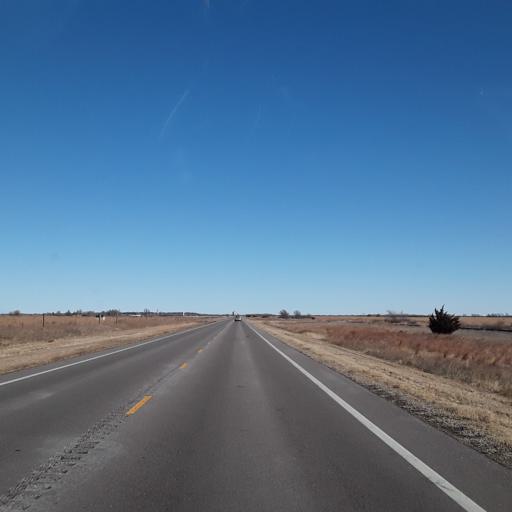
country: US
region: Kansas
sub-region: Pawnee County
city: Larned
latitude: 38.1341
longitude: -99.1590
